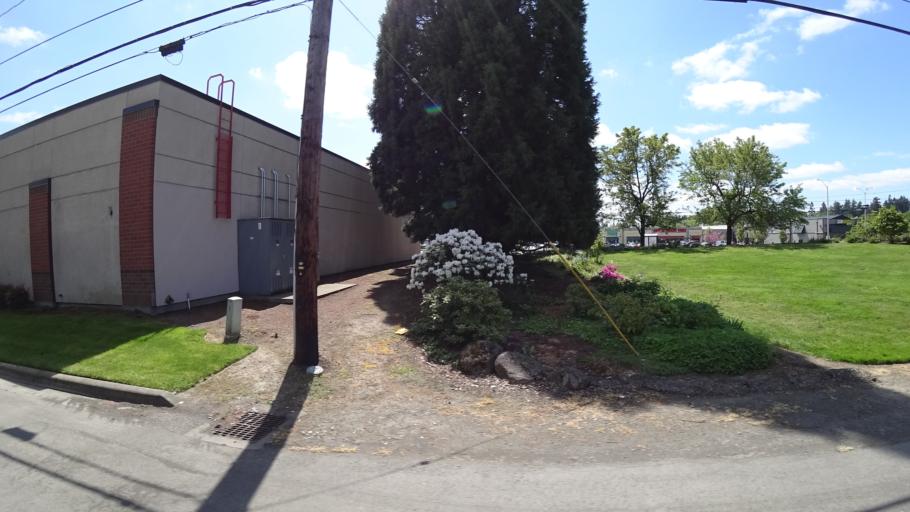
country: US
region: Oregon
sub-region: Washington County
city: Hillsboro
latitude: 45.5199
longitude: -123.0043
